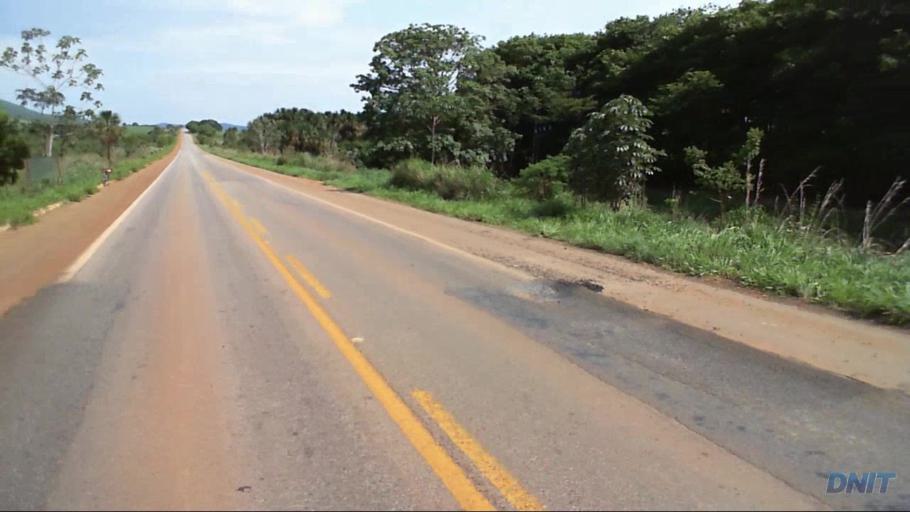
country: BR
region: Goias
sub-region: Barro Alto
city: Barro Alto
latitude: -15.0466
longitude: -48.8880
